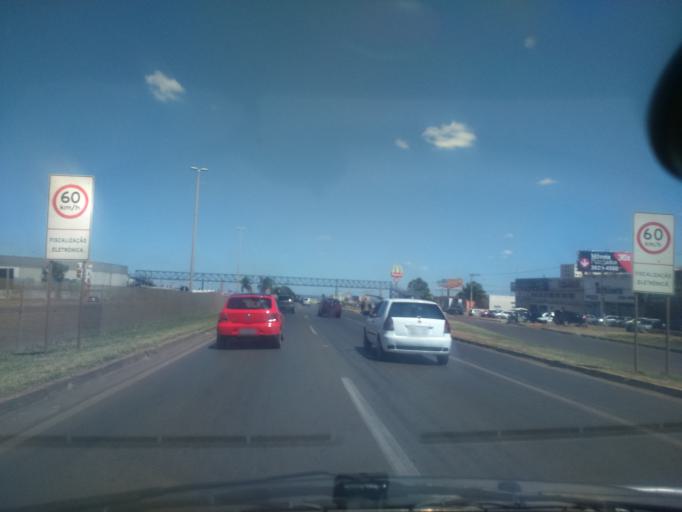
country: BR
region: Goias
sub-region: Luziania
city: Luziania
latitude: -16.0763
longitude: -47.9857
